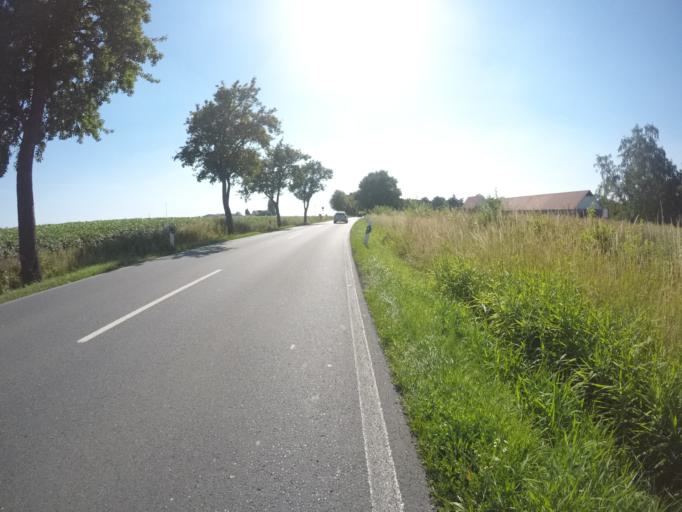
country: DE
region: North Rhine-Westphalia
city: Loehne
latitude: 52.1755
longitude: 8.7358
